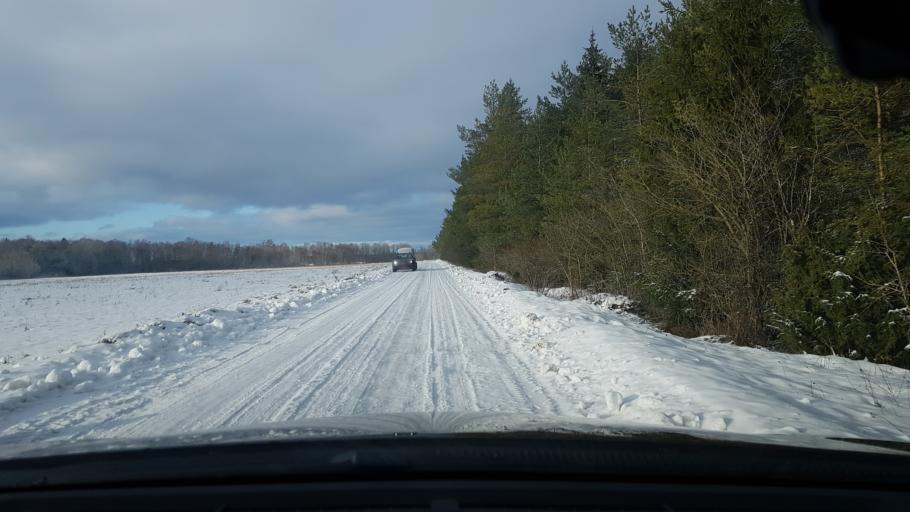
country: EE
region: Harju
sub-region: Keila linn
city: Keila
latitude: 59.2953
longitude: 24.2513
